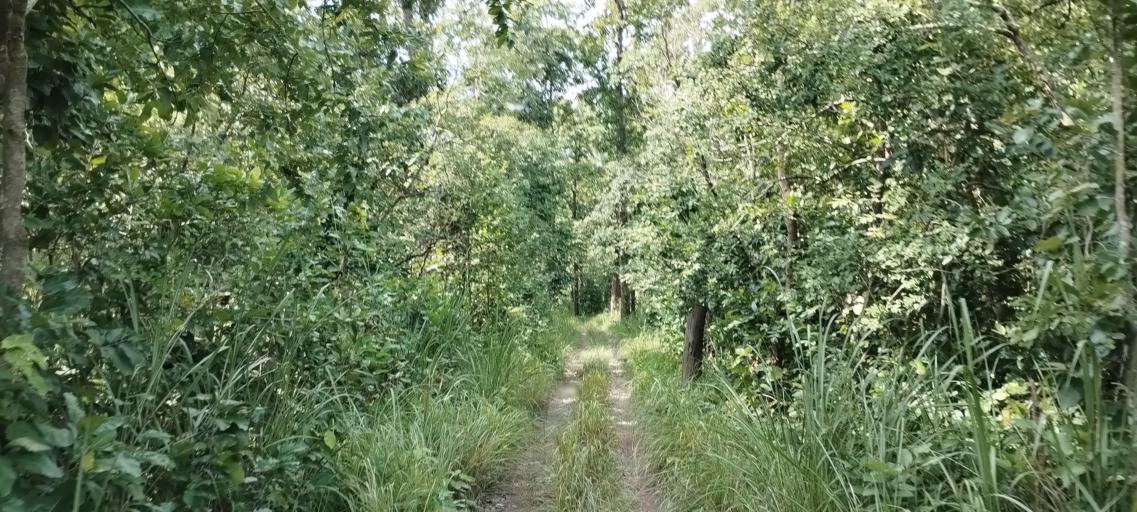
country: NP
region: Far Western
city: Tikapur
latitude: 28.5616
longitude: 81.2946
